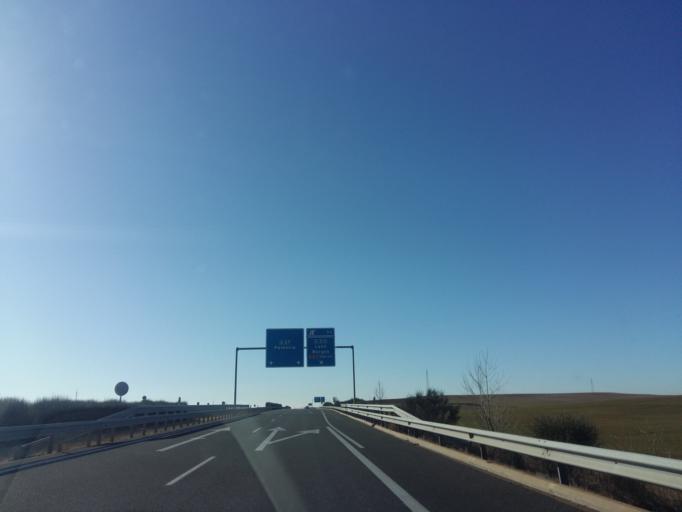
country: ES
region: Castille and Leon
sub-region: Provincia de Palencia
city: Abia de las Torres
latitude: 42.4135
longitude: -4.3887
